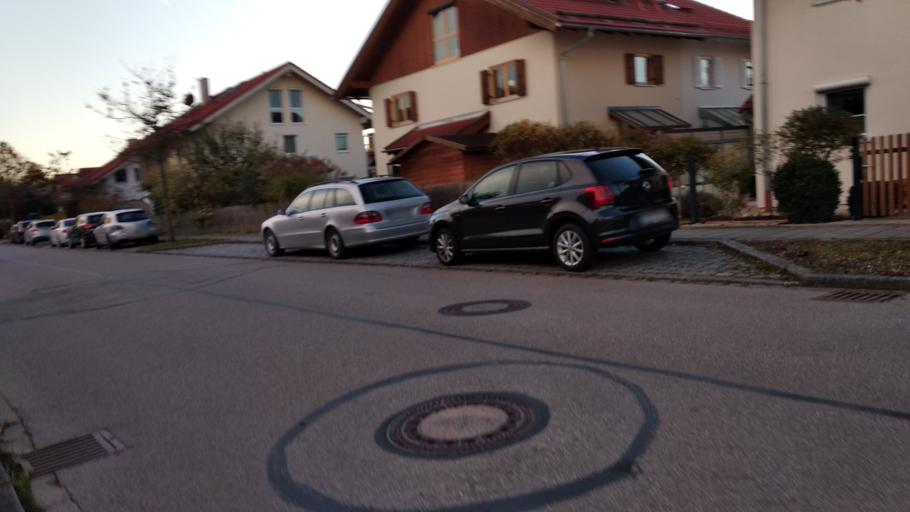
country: DE
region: Bavaria
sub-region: Upper Bavaria
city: Hohenkirchen-Siegertsbrunn
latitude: 48.0257
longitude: 11.7285
